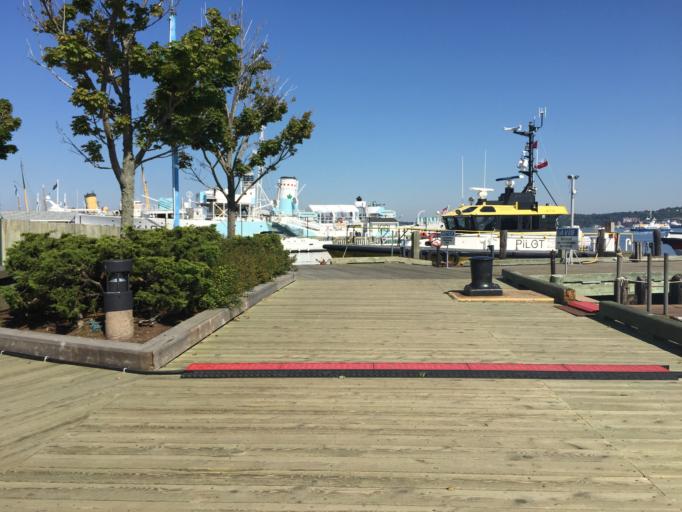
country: CA
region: Nova Scotia
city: Halifax
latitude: 44.6466
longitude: -63.5693
